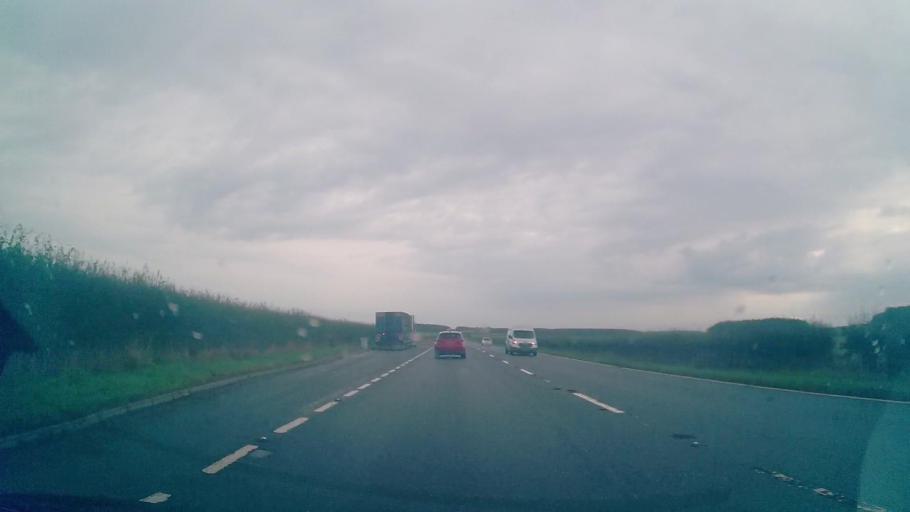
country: GB
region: Scotland
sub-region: Dumfries and Galloway
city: Annan
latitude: 55.0059
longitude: -3.3267
